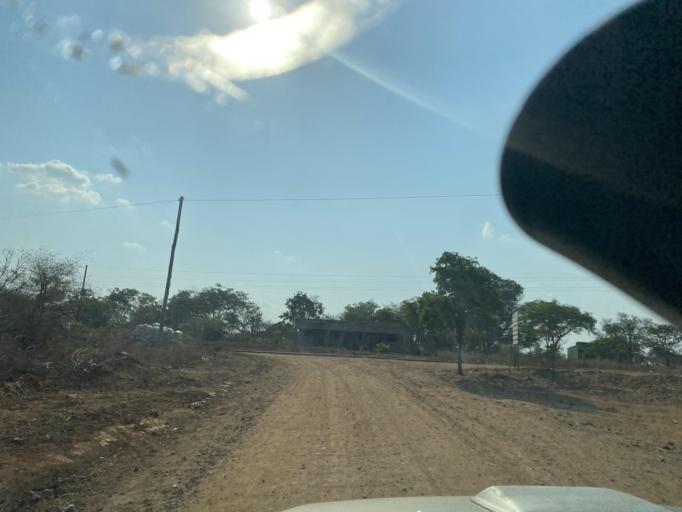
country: ZM
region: Lusaka
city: Chongwe
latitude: -15.3156
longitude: 28.7083
